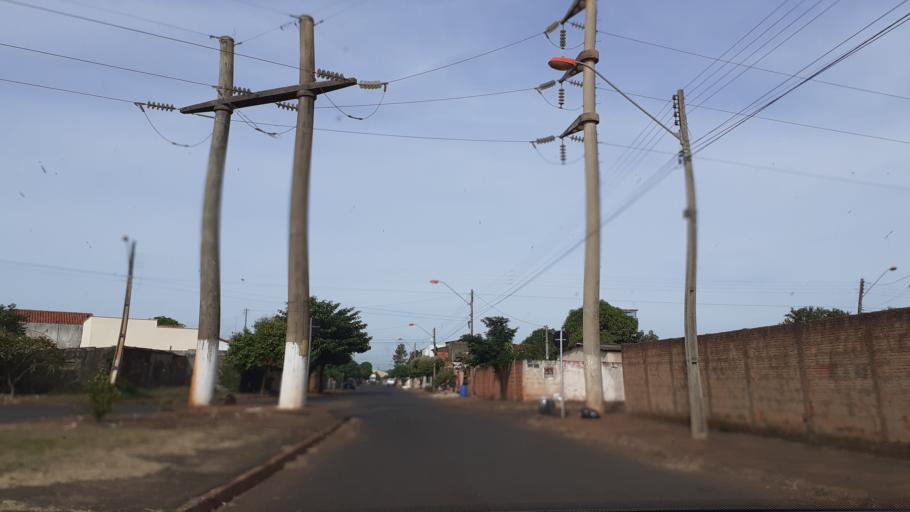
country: BR
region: Goias
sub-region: Itumbiara
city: Itumbiara
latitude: -18.4197
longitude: -49.2458
